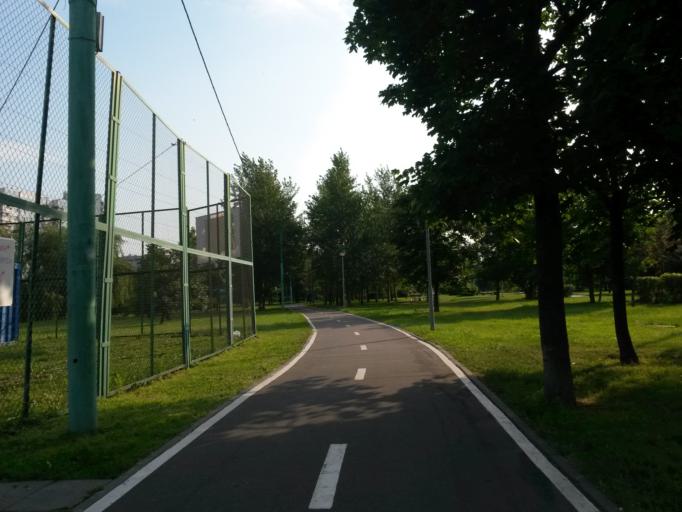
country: RU
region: Moscow
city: Brateyevo
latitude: 55.6454
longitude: 37.7599
